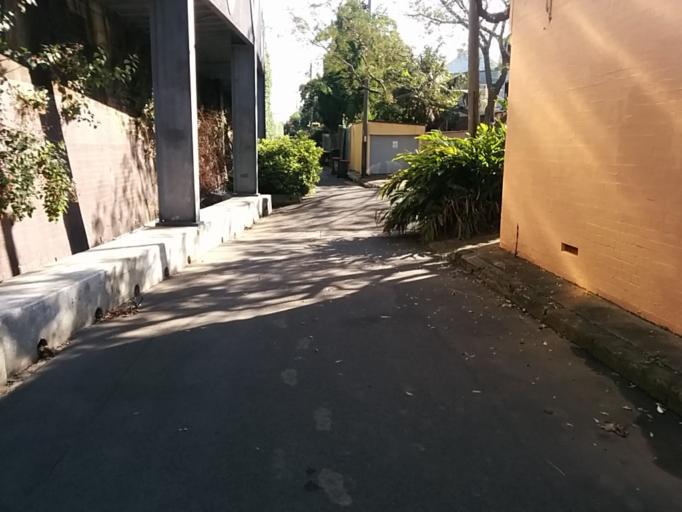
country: AU
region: New South Wales
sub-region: City of Sydney
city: Darlington
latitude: -33.8958
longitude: 151.1881
